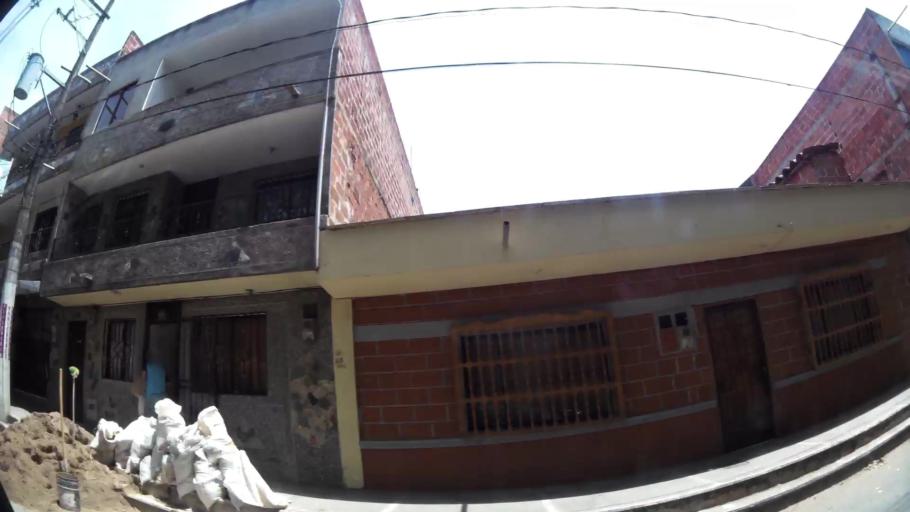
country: CO
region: Antioquia
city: Bello
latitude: 6.3405
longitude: -75.5639
